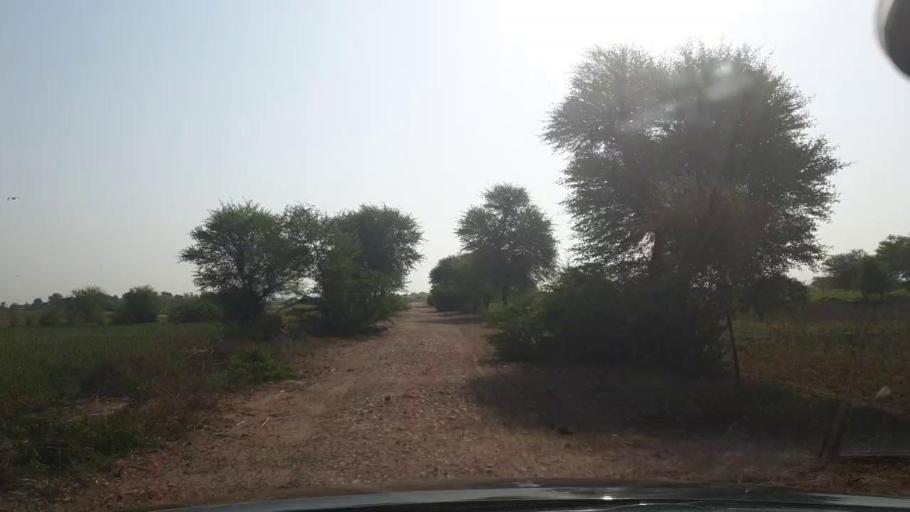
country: PK
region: Sindh
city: Tando Bago
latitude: 24.6513
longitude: 69.1579
